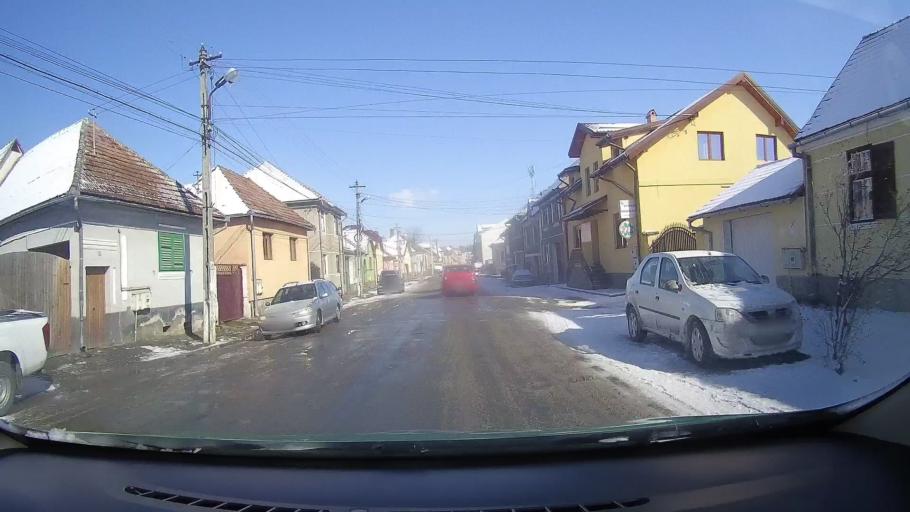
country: RO
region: Sibiu
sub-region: Comuna Avrig
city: Avrig
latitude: 45.7251
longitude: 24.3741
